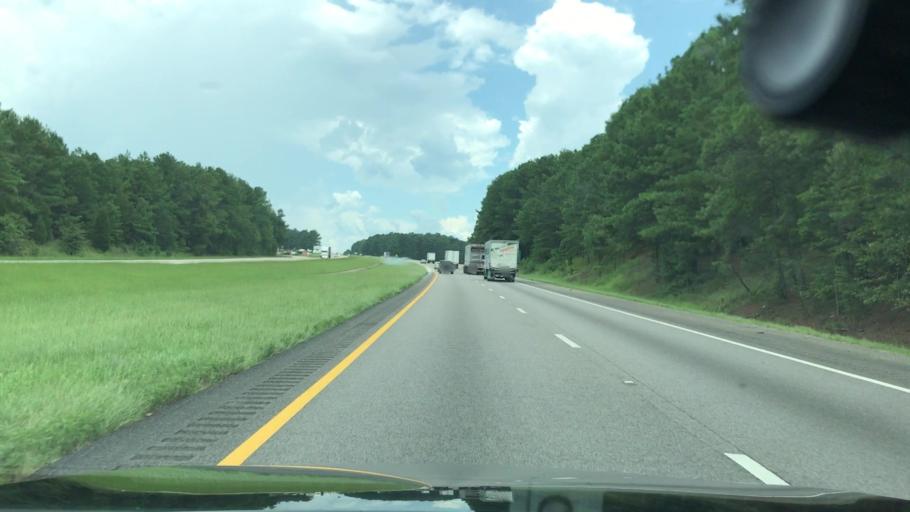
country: US
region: South Carolina
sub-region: Richland County
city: Blythewood
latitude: 34.3019
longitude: -80.9975
